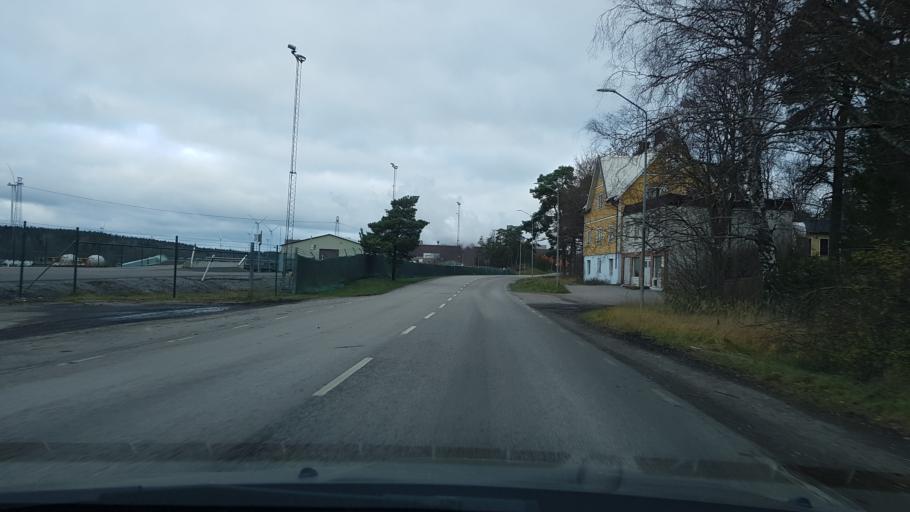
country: SE
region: Stockholm
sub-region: Norrtalje Kommun
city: Hallstavik
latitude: 60.0544
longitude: 18.5948
